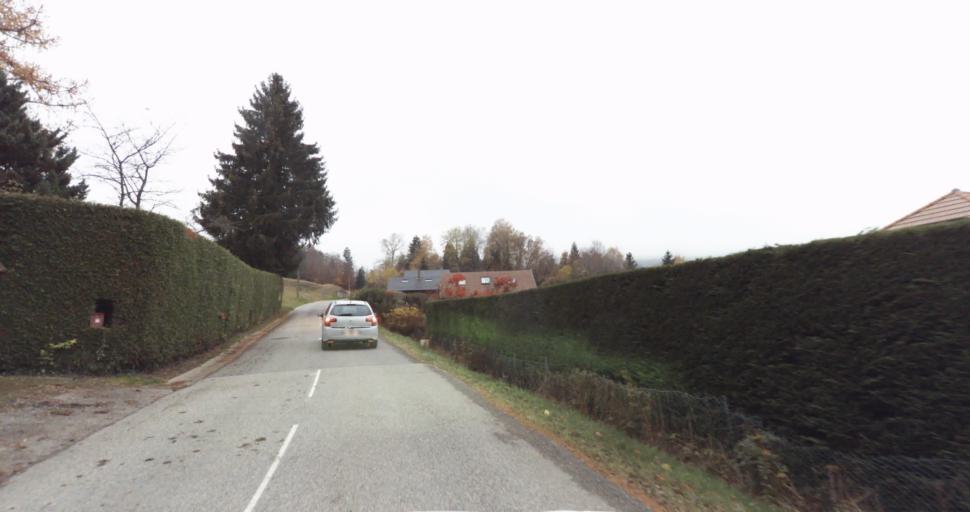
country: FR
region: Rhone-Alpes
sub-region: Departement de la Haute-Savoie
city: Saint-Jorioz
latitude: 45.7916
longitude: 6.1503
